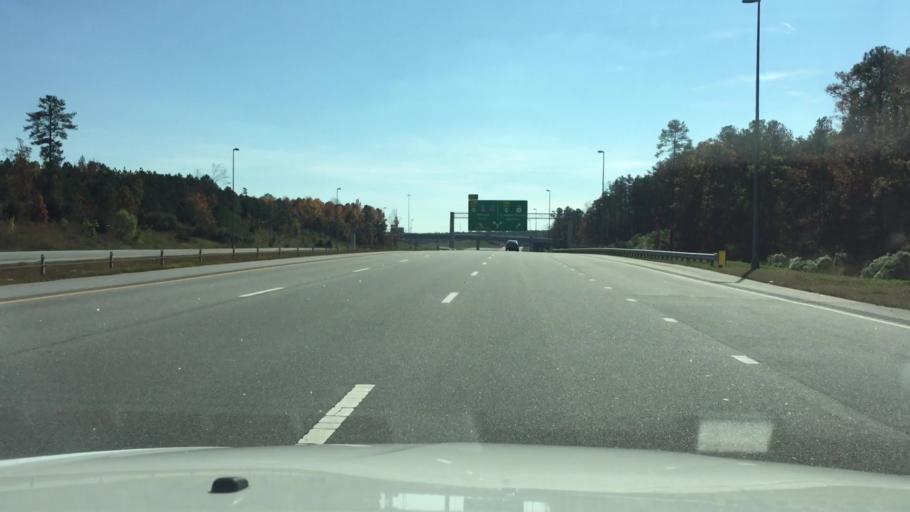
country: US
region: North Carolina
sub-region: Wake County
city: Morrisville
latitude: 35.8640
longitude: -78.8646
